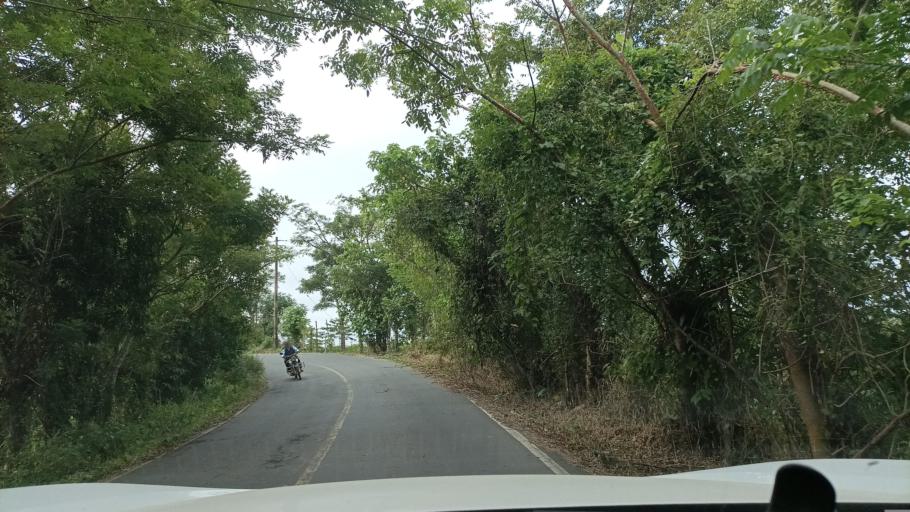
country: MX
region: Veracruz
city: Hidalgotitlan
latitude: 17.6898
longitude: -94.4522
